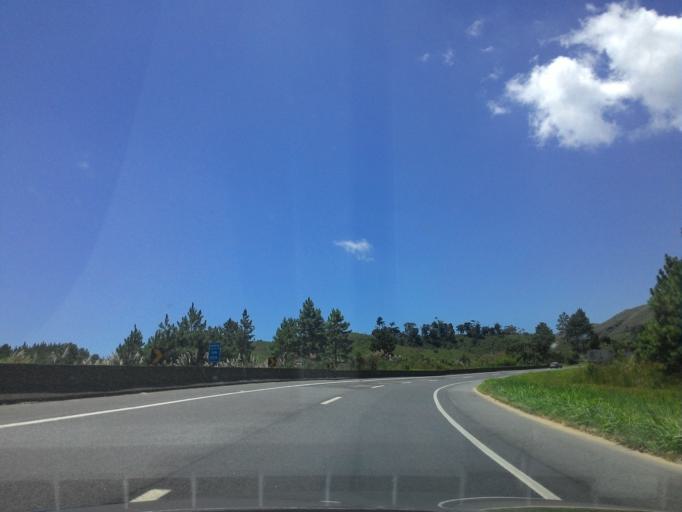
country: BR
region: Sao Paulo
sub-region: Cajati
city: Cajati
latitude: -24.9762
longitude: -48.5038
